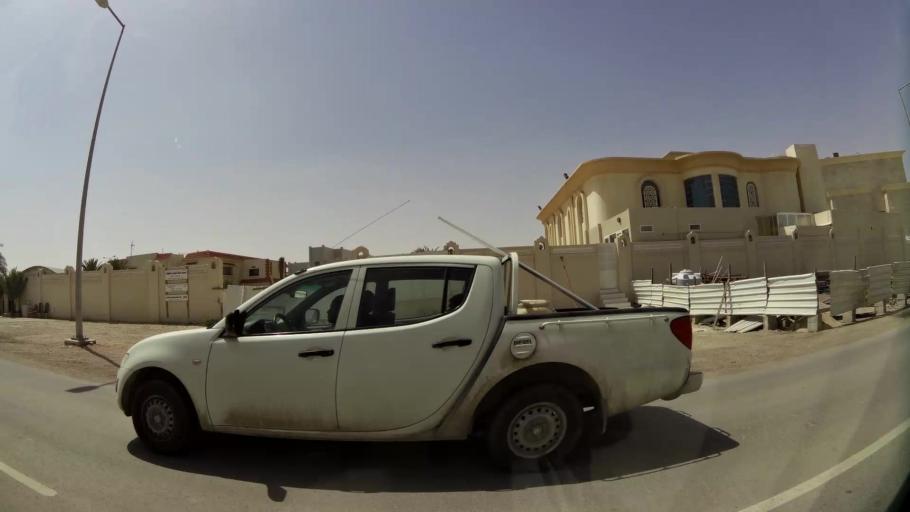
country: QA
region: Baladiyat Umm Salal
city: Umm Salal Muhammad
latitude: 25.3663
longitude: 51.4313
